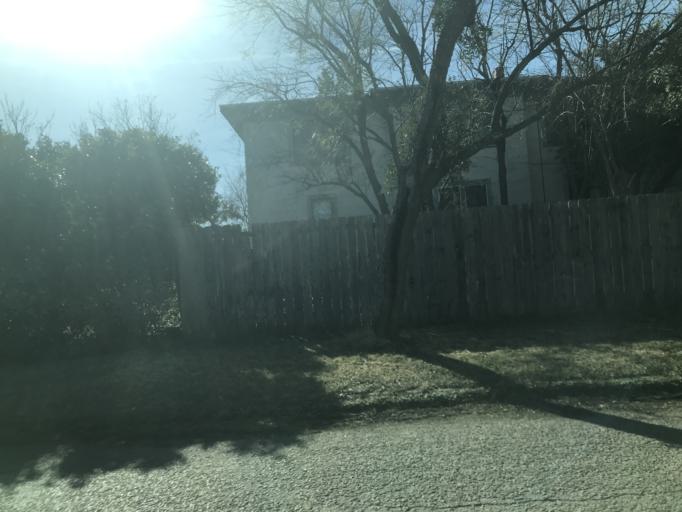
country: US
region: Texas
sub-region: Taylor County
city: Abilene
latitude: 32.4730
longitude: -99.7382
